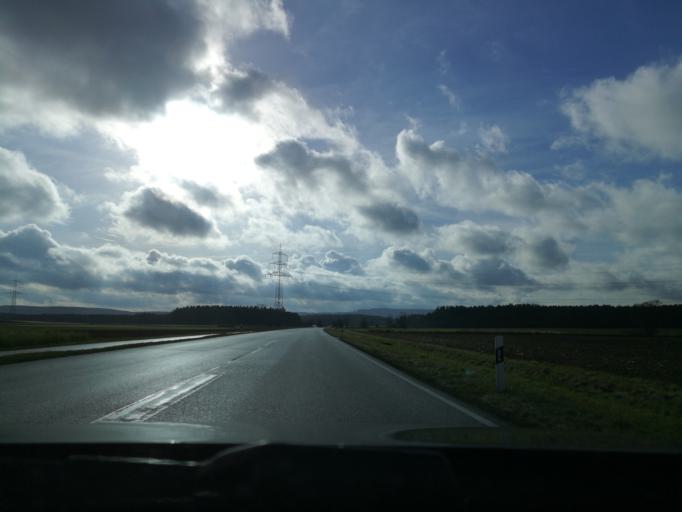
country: DE
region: Bavaria
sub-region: Regierungsbezirk Mittelfranken
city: Abenberg
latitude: 49.2399
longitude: 10.8967
